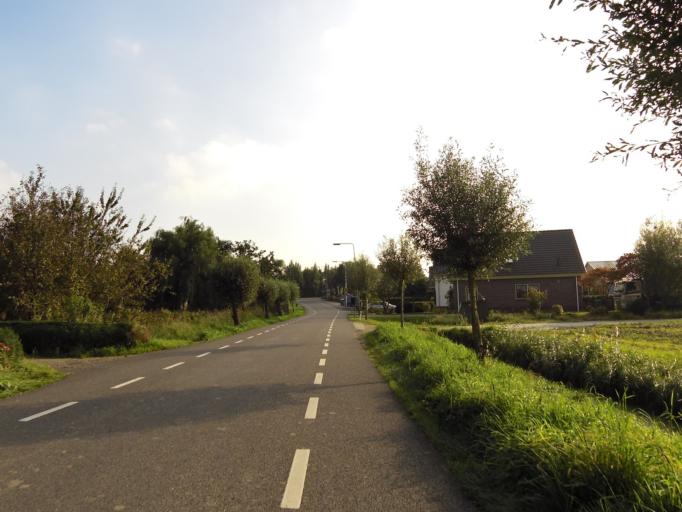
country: NL
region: South Holland
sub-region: Gemeente Rijnwoude
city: Benthuizen
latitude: 52.0961
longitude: 4.5570
